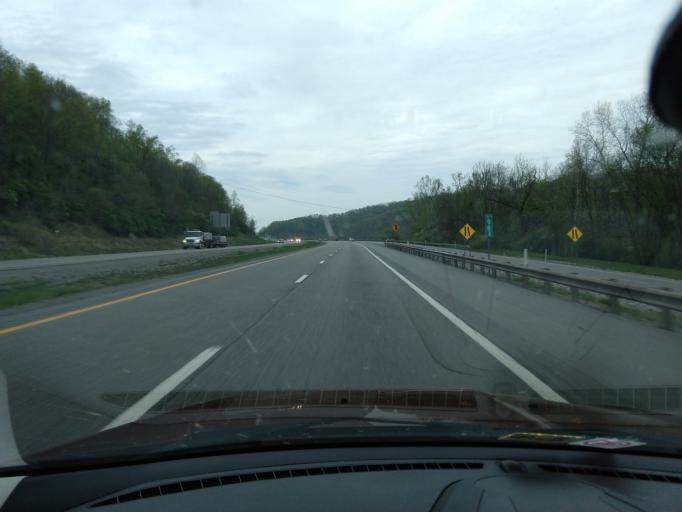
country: US
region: West Virginia
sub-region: Lewis County
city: Weston
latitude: 39.0240
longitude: -80.4257
